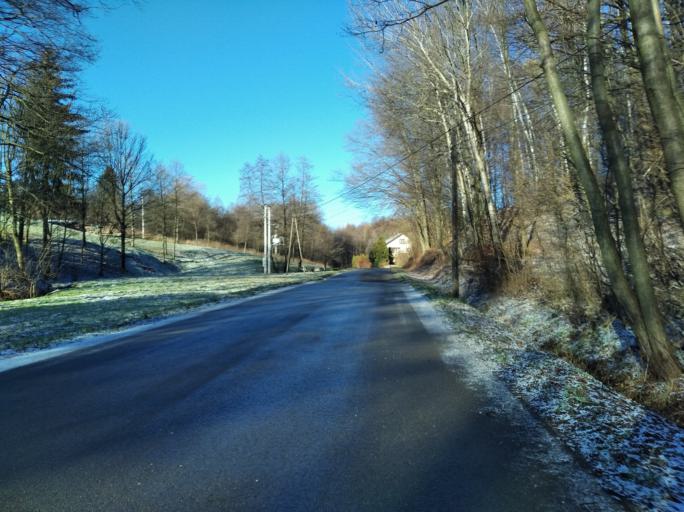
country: PL
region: Subcarpathian Voivodeship
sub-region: Powiat ropczycko-sedziszowski
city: Iwierzyce
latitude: 49.9625
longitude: 21.7574
